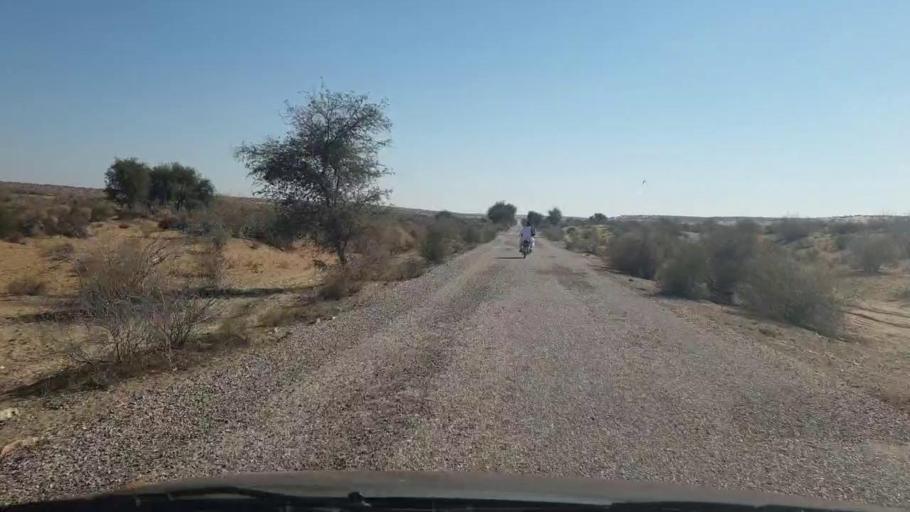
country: PK
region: Sindh
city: Bozdar
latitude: 27.0352
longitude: 68.6975
